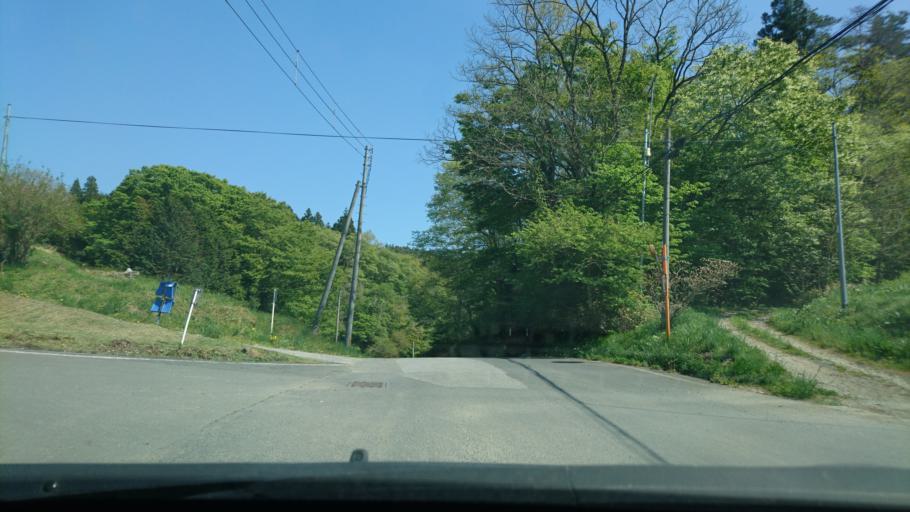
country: JP
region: Iwate
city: Ichinoseki
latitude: 38.9368
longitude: 141.2776
